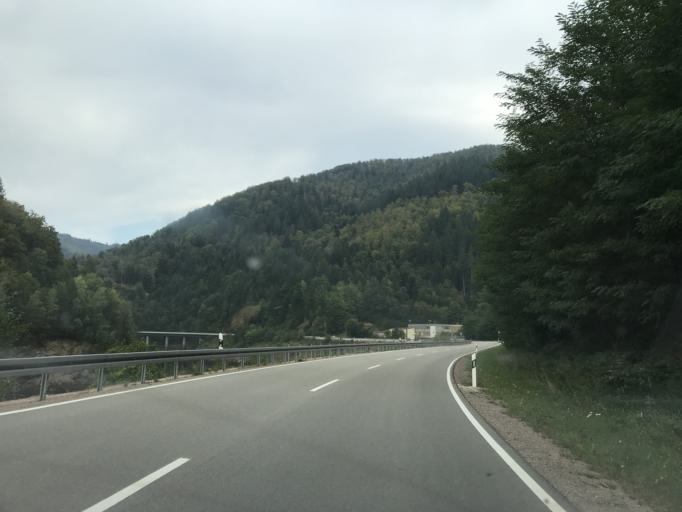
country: DE
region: Baden-Wuerttemberg
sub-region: Freiburg Region
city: Hasel
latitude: 47.6499
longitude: 7.9231
